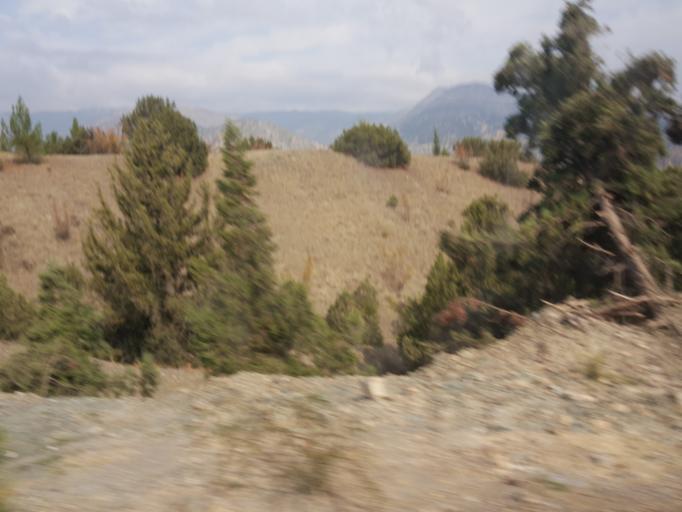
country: TR
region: Corum
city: Kamil
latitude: 41.1106
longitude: 34.7436
